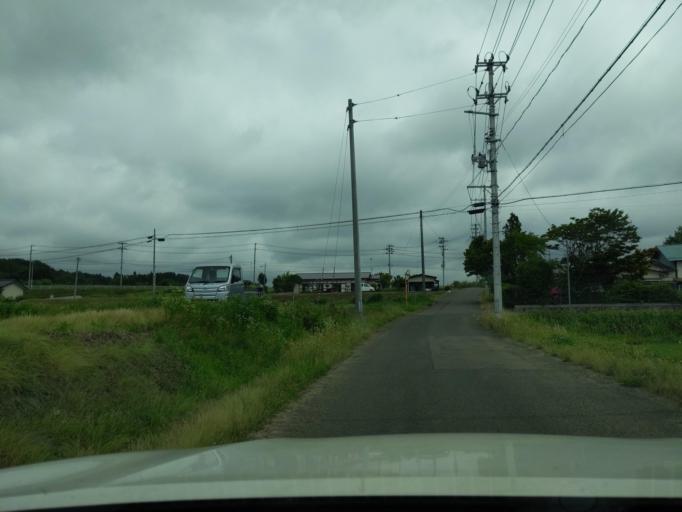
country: JP
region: Fukushima
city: Koriyama
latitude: 37.4586
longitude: 140.3102
